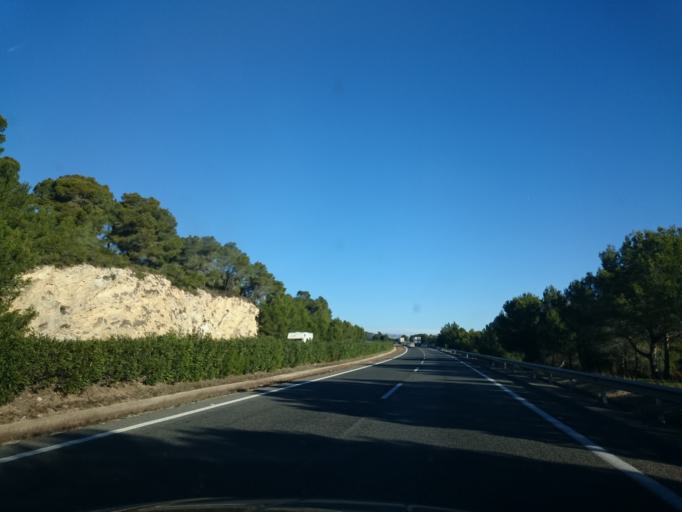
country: ES
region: Catalonia
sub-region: Provincia de Tarragona
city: L'Ampolla
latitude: 40.8338
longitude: 0.7406
